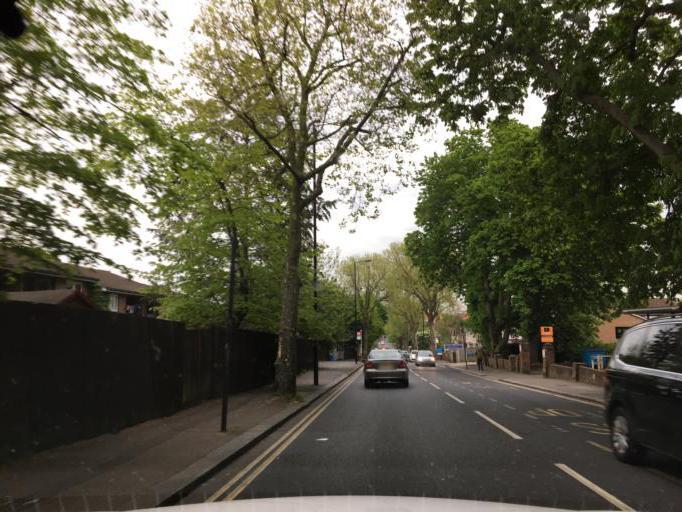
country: GB
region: England
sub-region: Greater London
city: Bromley
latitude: 51.4316
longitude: 0.0219
